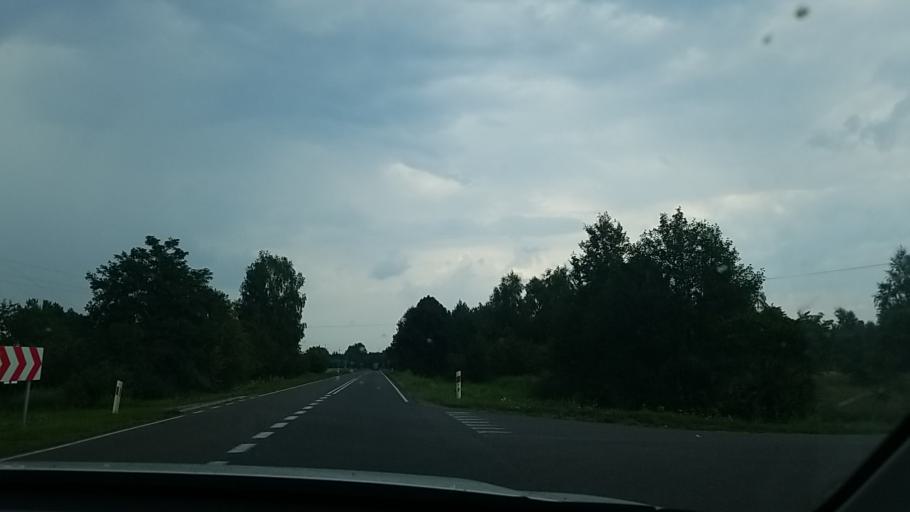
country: PL
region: Lublin Voivodeship
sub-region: Powiat leczynski
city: Cycow
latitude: 51.2380
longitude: 23.0868
